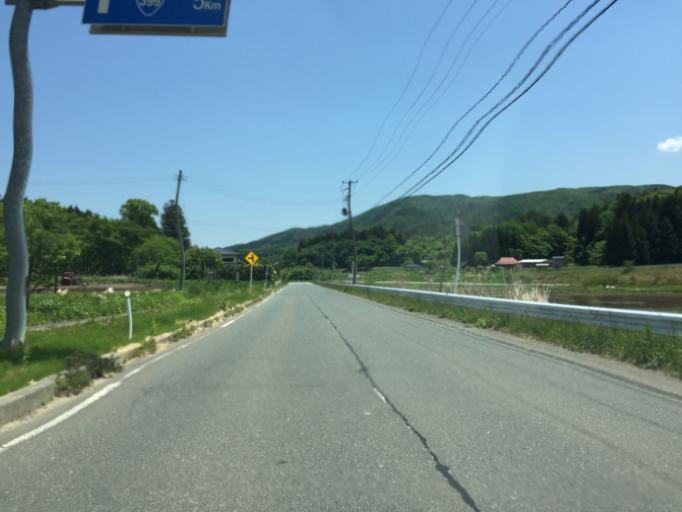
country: JP
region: Fukushima
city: Funehikimachi-funehiki
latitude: 37.5088
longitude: 140.7189
